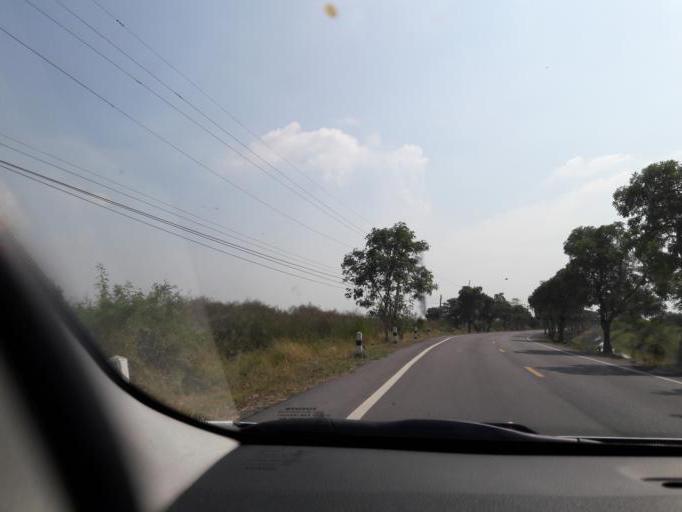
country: TH
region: Ang Thong
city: Wiset Chaichan
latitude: 14.5621
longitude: 100.3880
